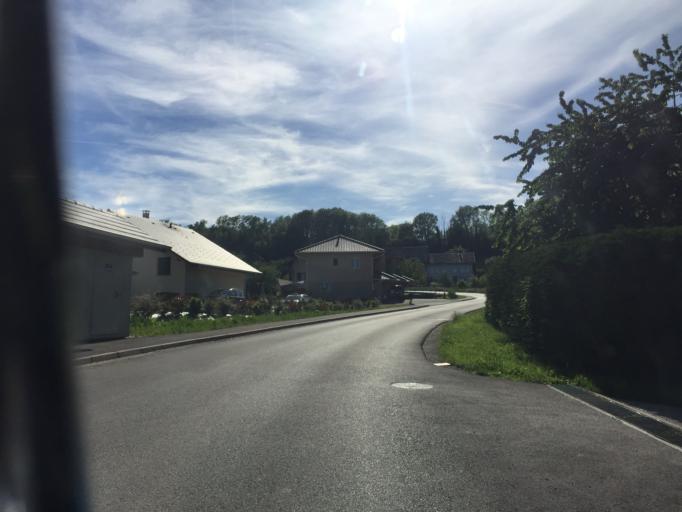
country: FR
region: Rhone-Alpes
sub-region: Departement de la Haute-Savoie
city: Sillingy
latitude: 45.9375
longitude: 6.0245
